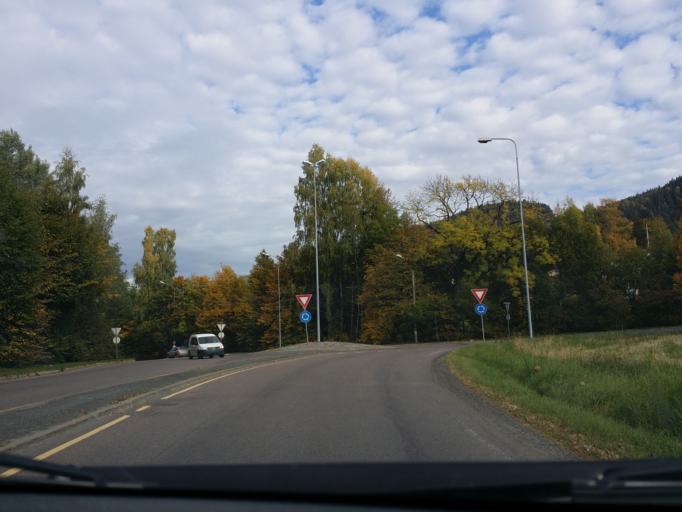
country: NO
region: Akershus
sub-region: Baerum
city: Sandvika
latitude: 59.9168
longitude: 10.4965
